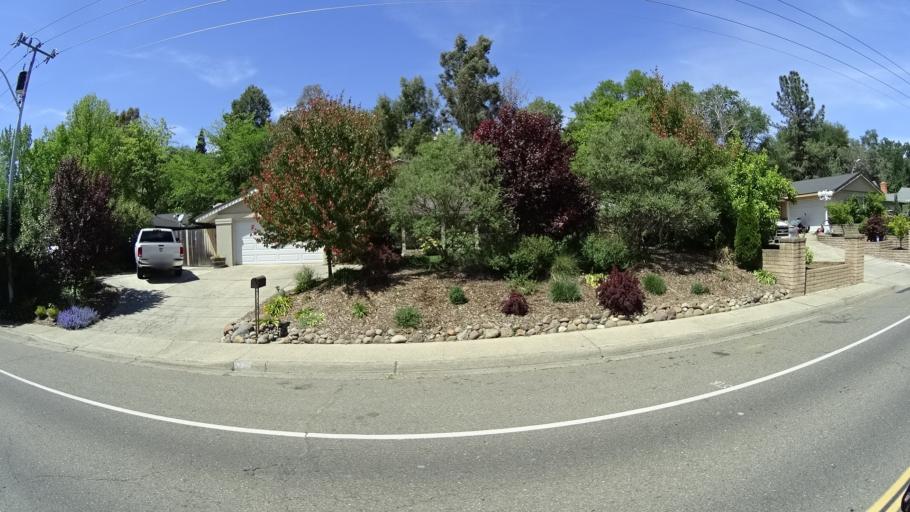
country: US
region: California
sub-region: Placer County
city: Rocklin
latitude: 38.8056
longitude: -121.2462
